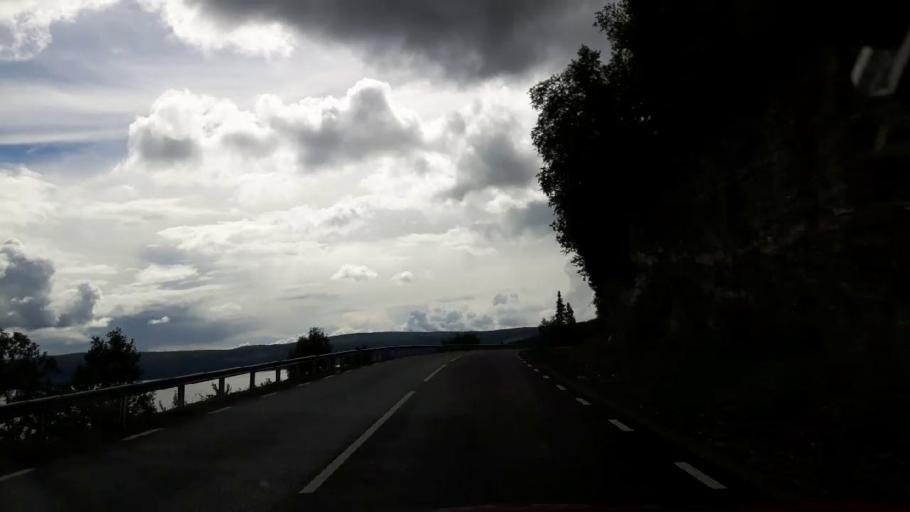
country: NO
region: Nord-Trondelag
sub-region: Royrvik
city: Royrvik
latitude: 64.8260
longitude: 14.0786
